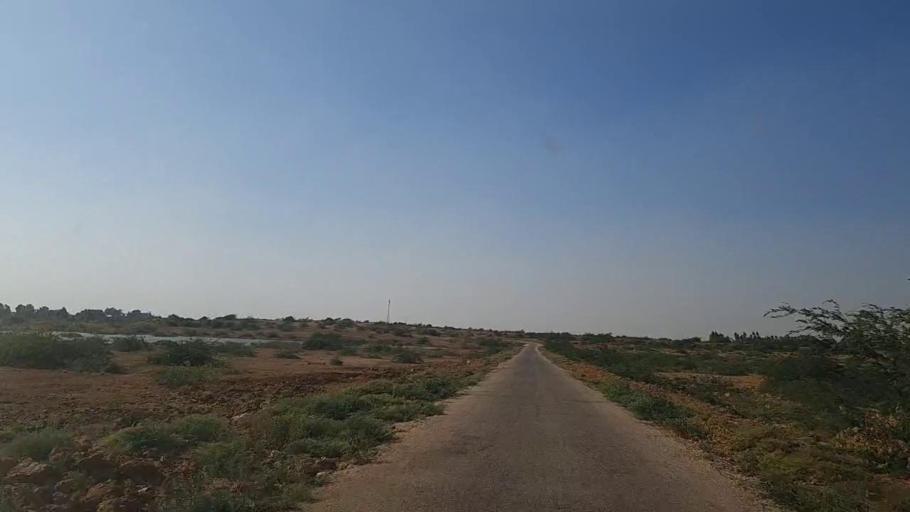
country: PK
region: Sindh
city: Daro Mehar
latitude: 24.9995
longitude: 68.1261
